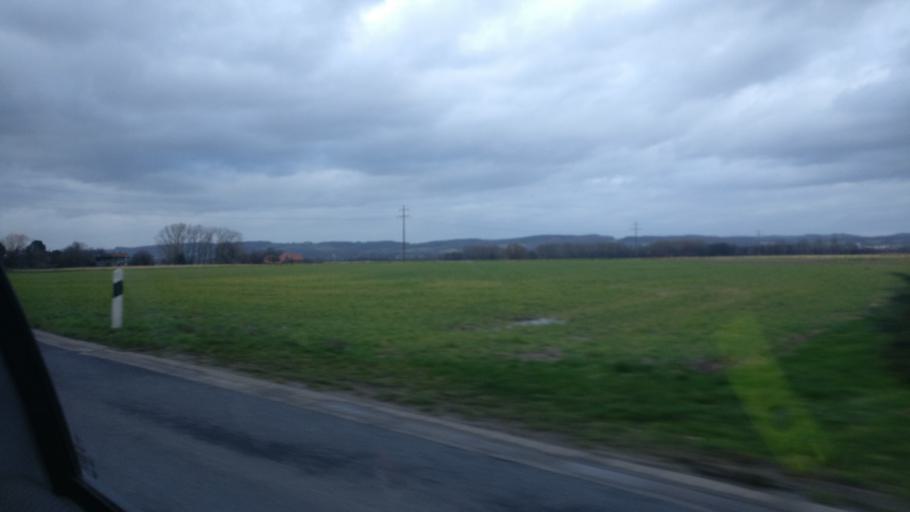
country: DE
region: North Rhine-Westphalia
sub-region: Regierungsbezirk Detmold
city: Lage
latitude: 52.0189
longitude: 8.7861
